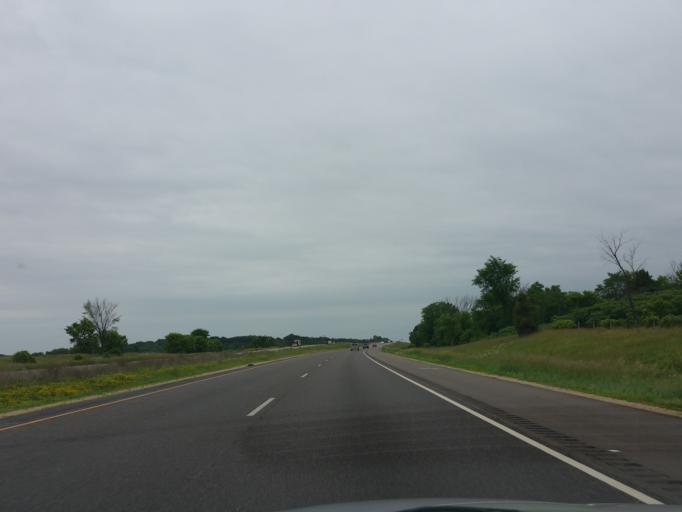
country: US
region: Wisconsin
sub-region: Eau Claire County
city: Eau Claire
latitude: 44.8198
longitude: -91.5681
